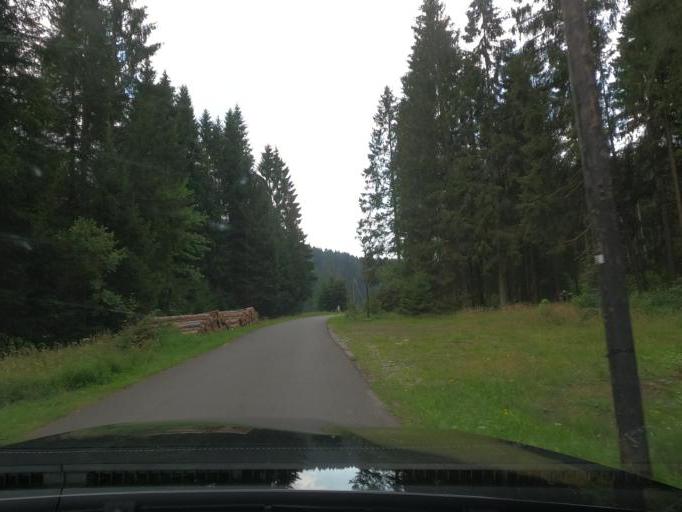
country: DE
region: Lower Saxony
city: Wildemann
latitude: 51.7943
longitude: 10.3009
